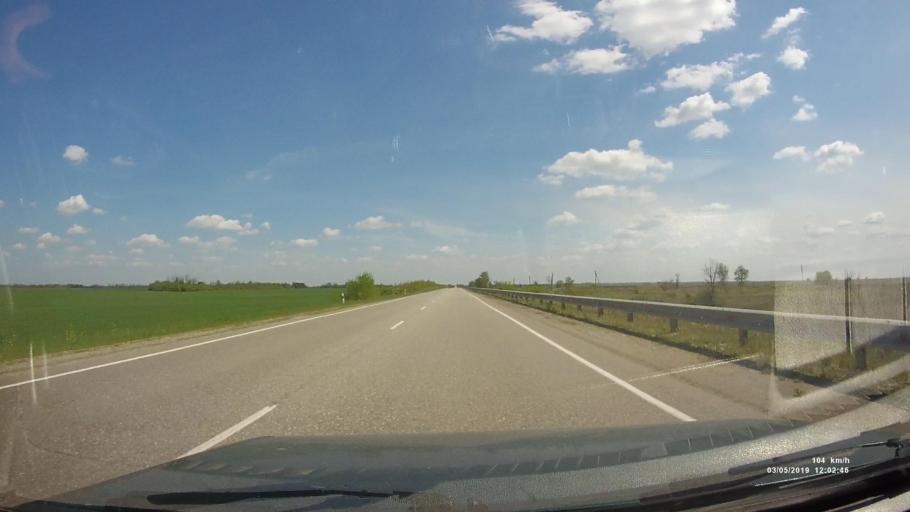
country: RU
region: Rostov
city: Bagayevskaya
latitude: 47.2725
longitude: 40.3750
